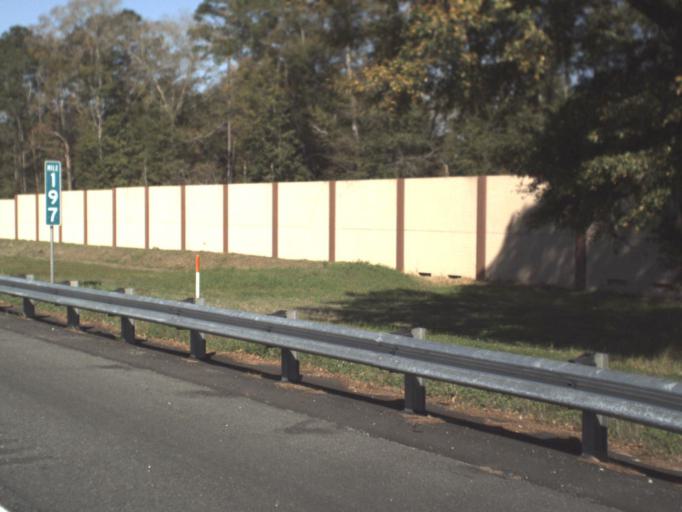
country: US
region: Florida
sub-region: Leon County
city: Tallahassee
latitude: 30.4785
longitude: -84.3343
